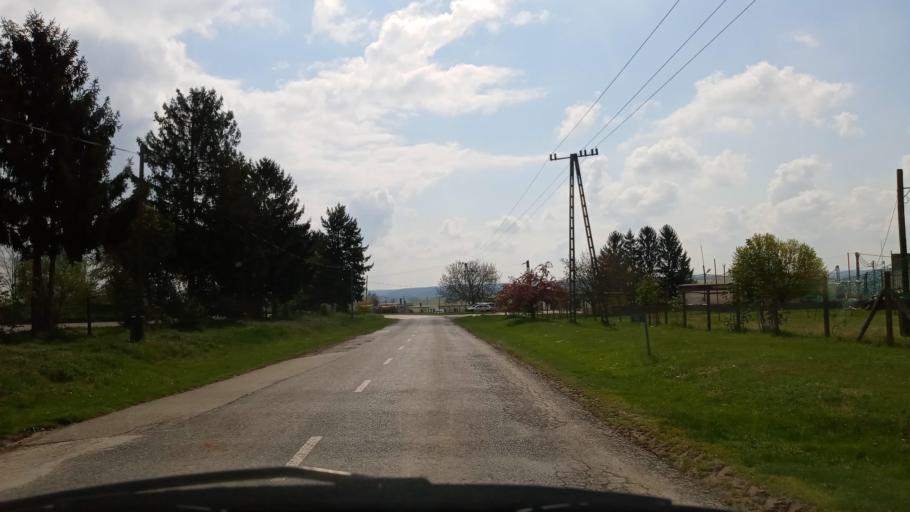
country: HU
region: Baranya
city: Pecsvarad
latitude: 46.1076
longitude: 18.5195
